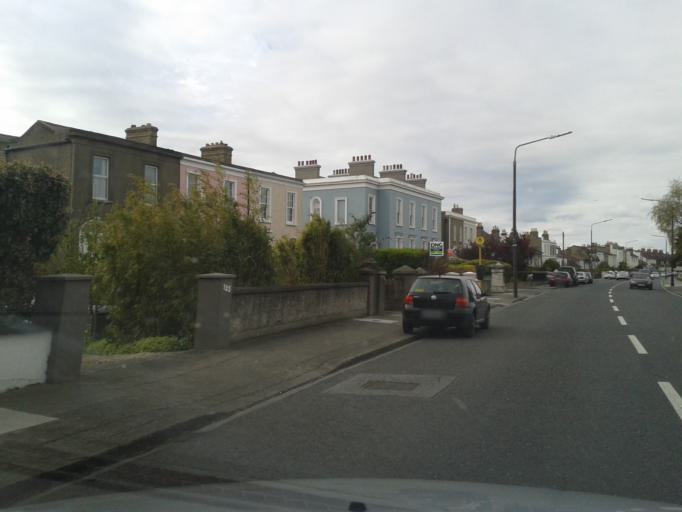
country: IE
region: Leinster
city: Sandymount
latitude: 53.3257
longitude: -6.2074
